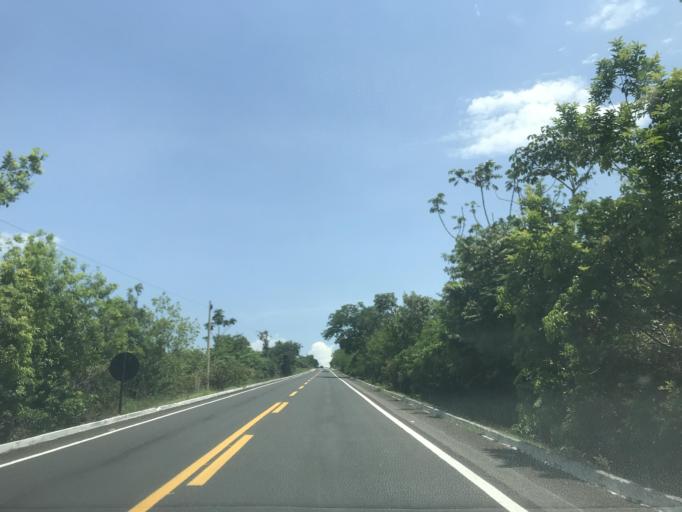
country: BR
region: Goias
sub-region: Bela Vista De Goias
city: Bela Vista de Goias
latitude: -17.1246
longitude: -48.6681
